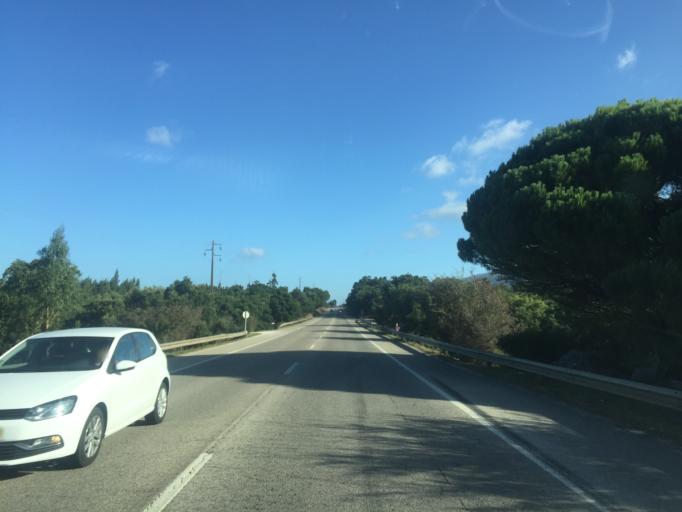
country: PT
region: Leiria
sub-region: Alcobaca
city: Aljubarrota
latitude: 39.5151
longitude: -8.9193
